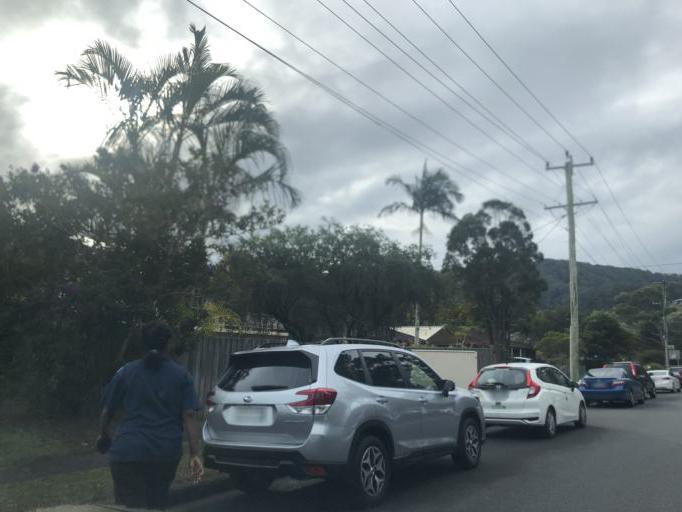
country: AU
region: New South Wales
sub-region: Coffs Harbour
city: Coffs Harbour
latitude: -30.2827
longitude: 153.1117
